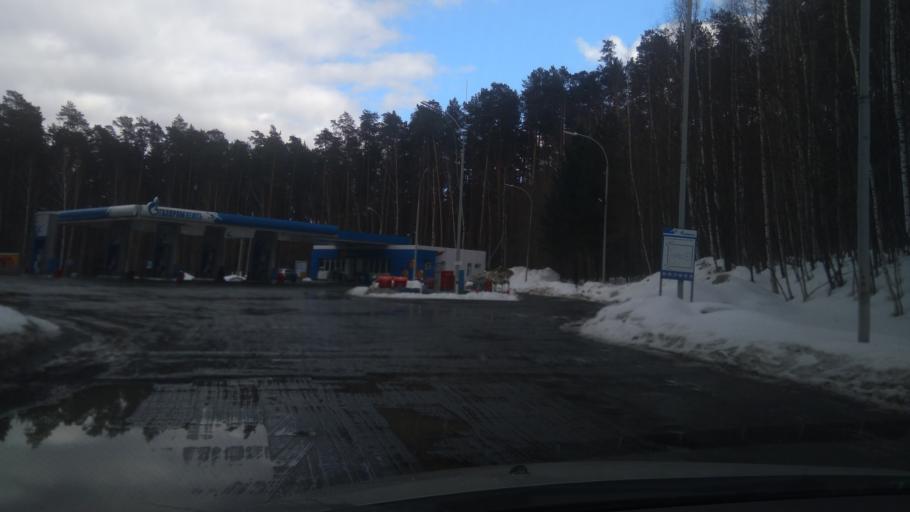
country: RU
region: Sverdlovsk
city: Shirokaya Rechka
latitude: 56.8249
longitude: 60.4671
